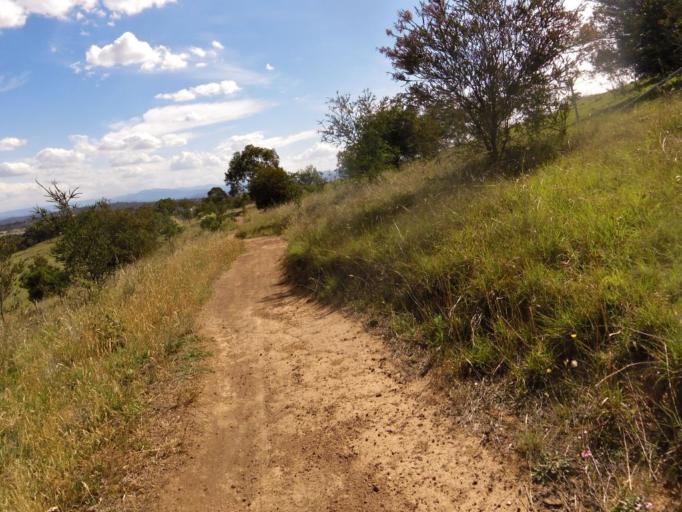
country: AU
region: Australian Capital Territory
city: Belconnen
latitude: -35.1624
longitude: 149.0744
